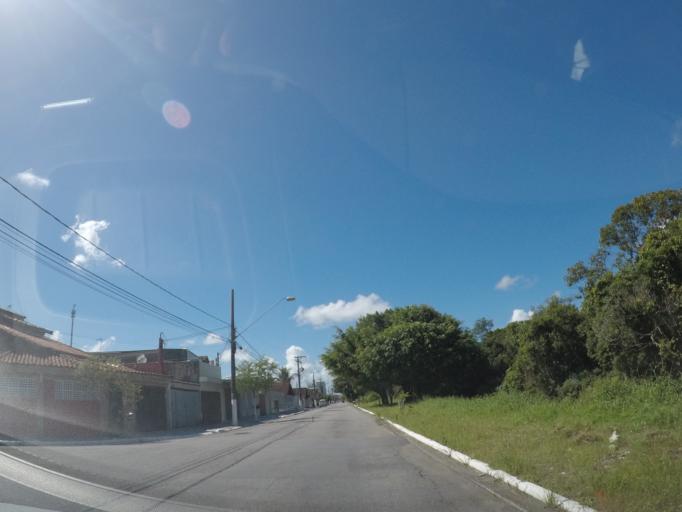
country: BR
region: Sao Paulo
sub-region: Praia Grande
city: Praia Grande
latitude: -24.0312
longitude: -46.5003
